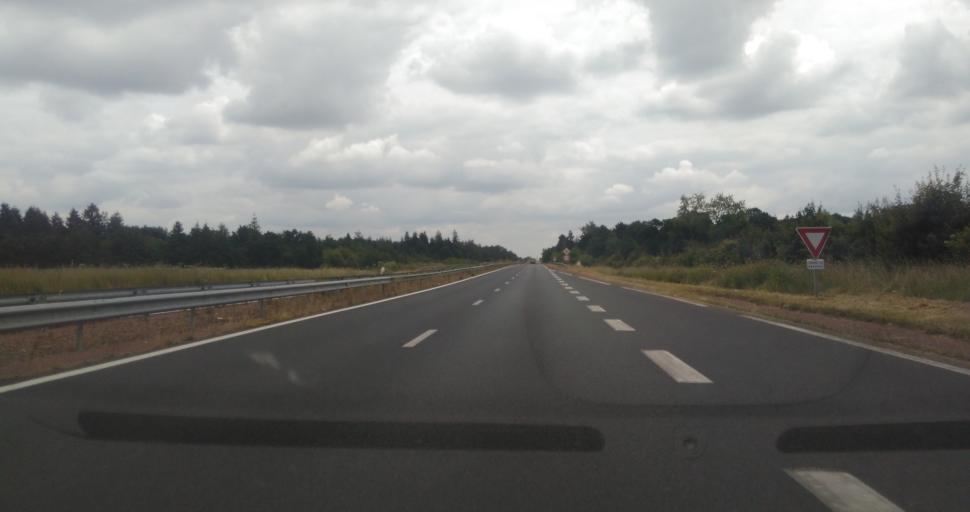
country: FR
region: Pays de la Loire
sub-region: Departement de la Vendee
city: Bournezeau
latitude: 46.6519
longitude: -1.2262
